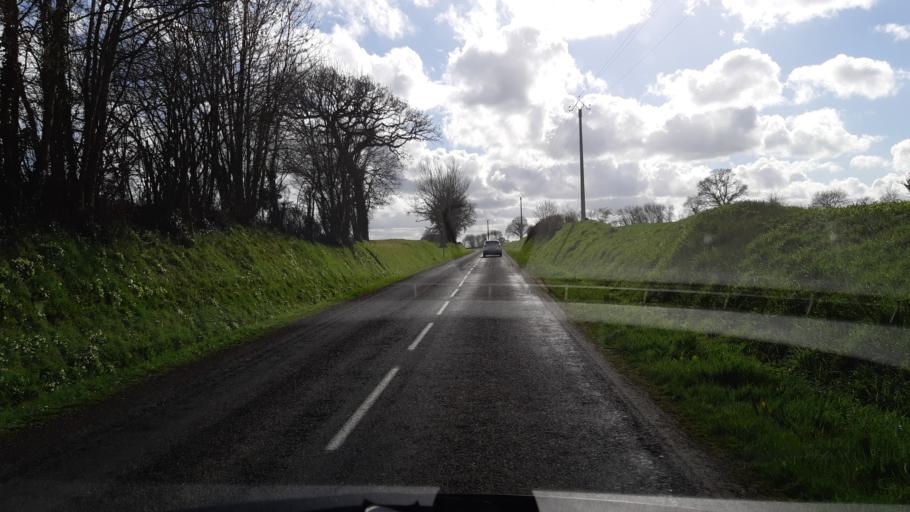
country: FR
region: Lower Normandy
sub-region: Departement de la Manche
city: Agneaux
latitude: 49.0242
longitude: -1.1563
